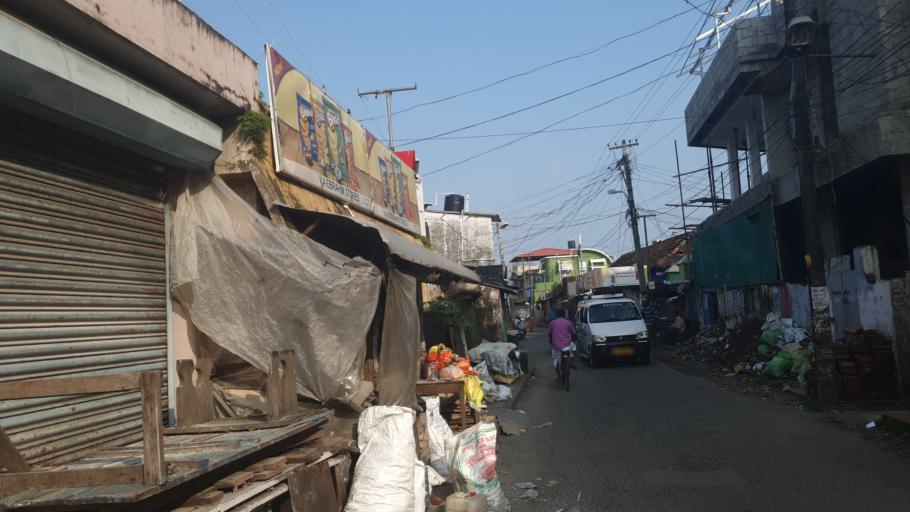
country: IN
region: Kerala
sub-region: Ernakulam
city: Cochin
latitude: 9.9629
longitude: 76.2519
